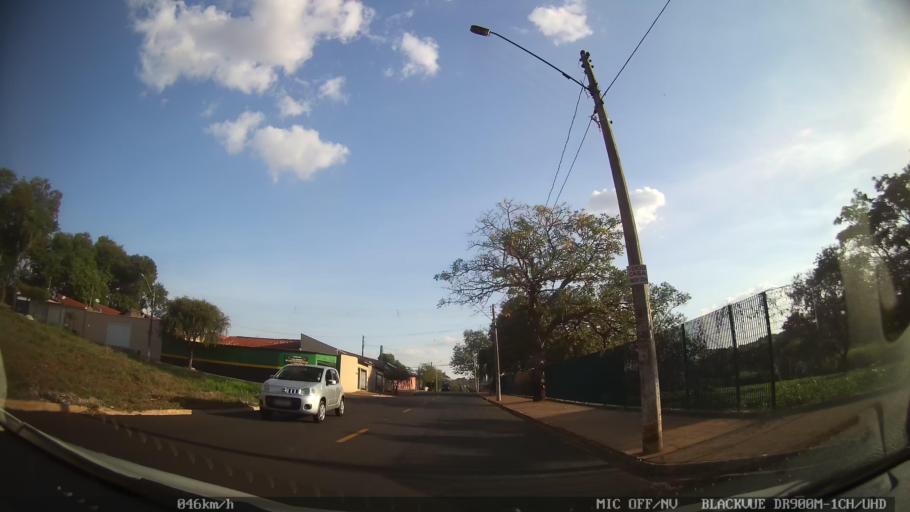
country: BR
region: Sao Paulo
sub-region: Ribeirao Preto
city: Ribeirao Preto
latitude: -21.1494
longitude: -47.8381
